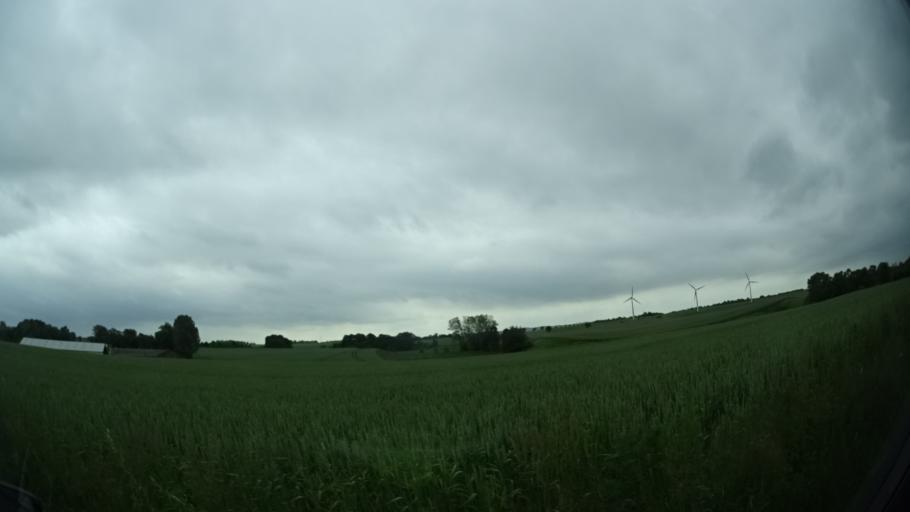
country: DK
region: Central Jutland
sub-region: Arhus Kommune
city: Tranbjerg
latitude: 56.0716
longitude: 10.0957
